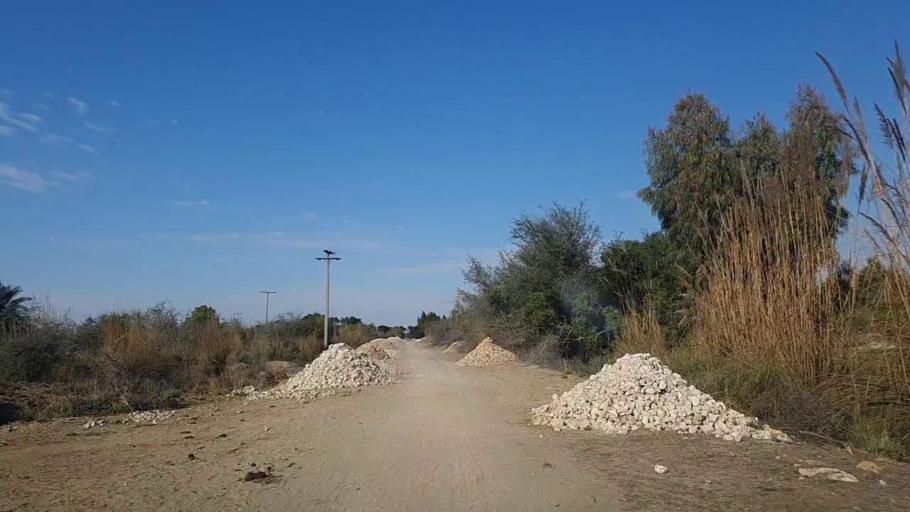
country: PK
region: Sindh
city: Jam Sahib
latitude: 26.3060
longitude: 68.8141
